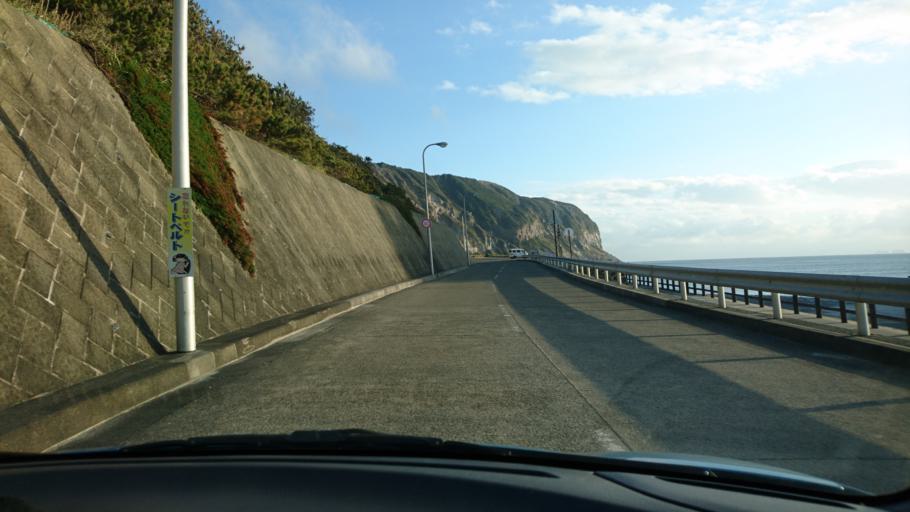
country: JP
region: Shizuoka
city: Shimoda
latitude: 34.3638
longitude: 139.2431
